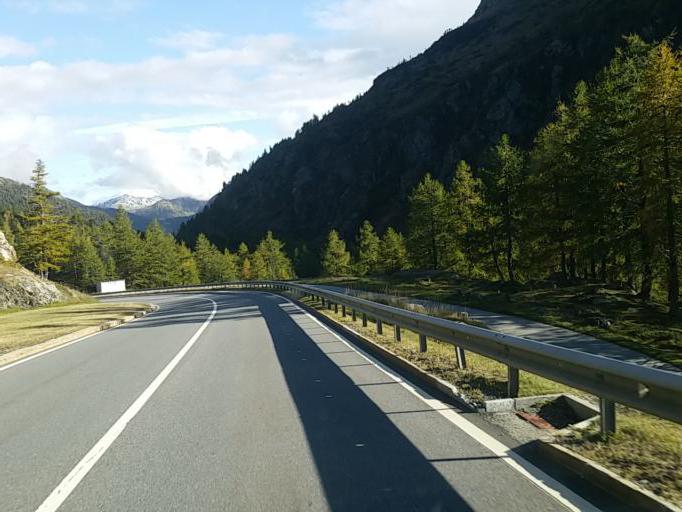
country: CH
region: Valais
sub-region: Brig District
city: Brig
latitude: 46.2250
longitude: 8.0167
